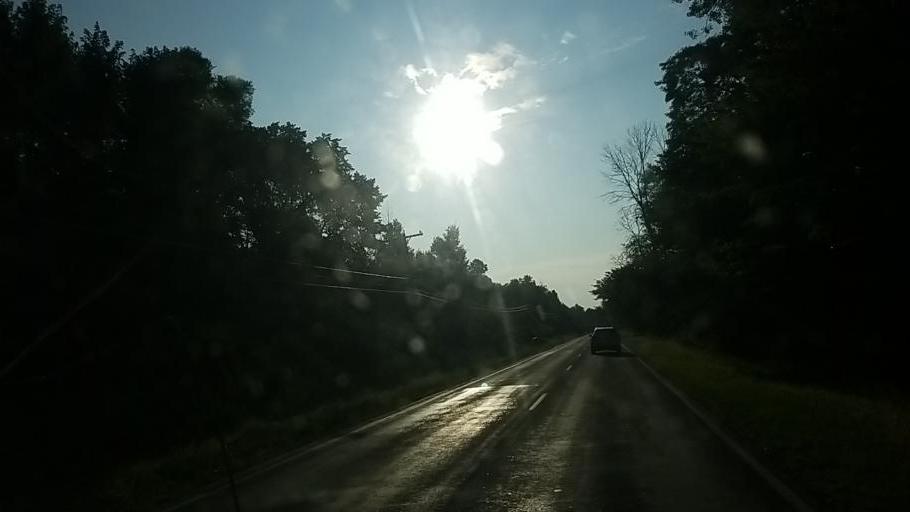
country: US
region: Michigan
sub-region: Montcalm County
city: Stanton
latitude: 43.2498
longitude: -85.0868
